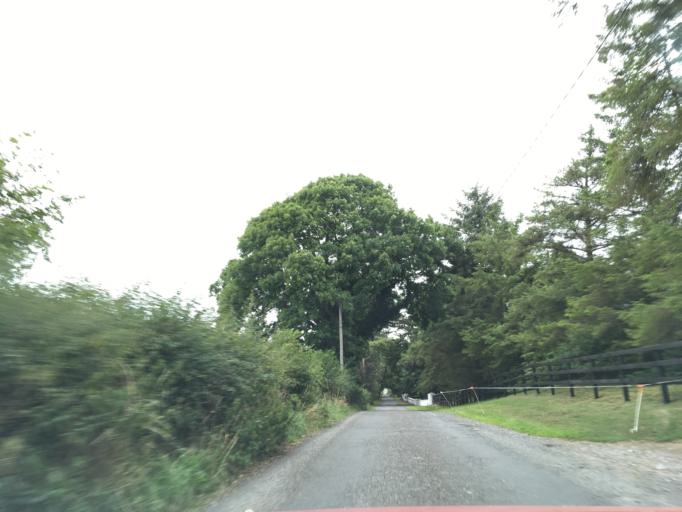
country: IE
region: Munster
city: Cashel
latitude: 52.4718
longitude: -7.9131
